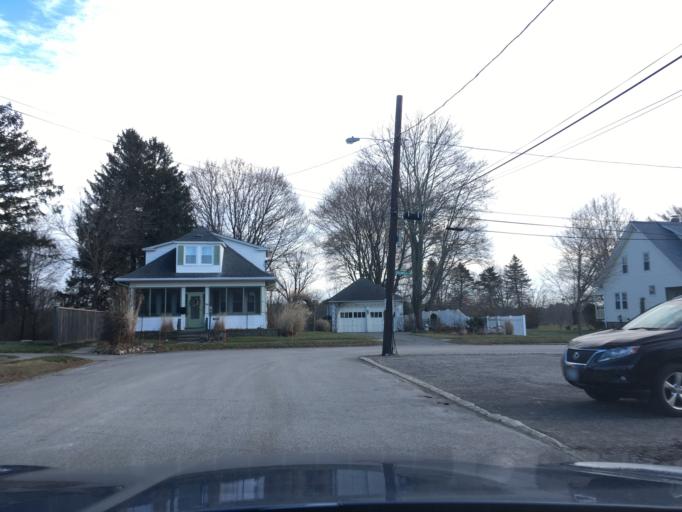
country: US
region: Rhode Island
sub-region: Kent County
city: East Greenwich
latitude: 41.6530
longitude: -71.4554
